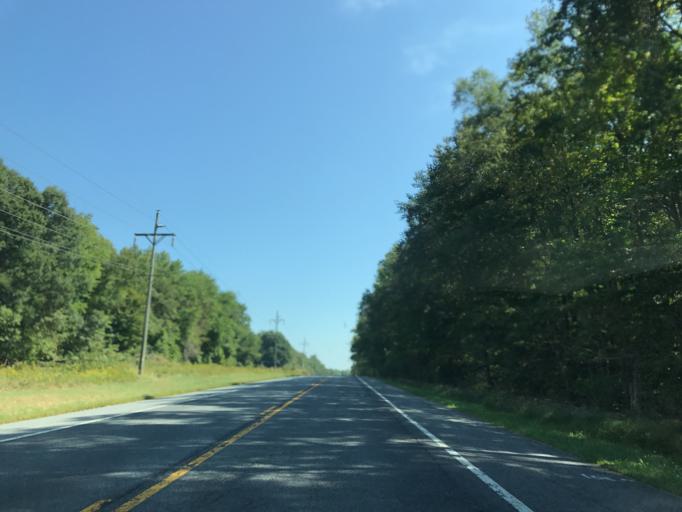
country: US
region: Maryland
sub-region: Queen Anne's County
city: Kingstown
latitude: 39.2643
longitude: -75.8869
